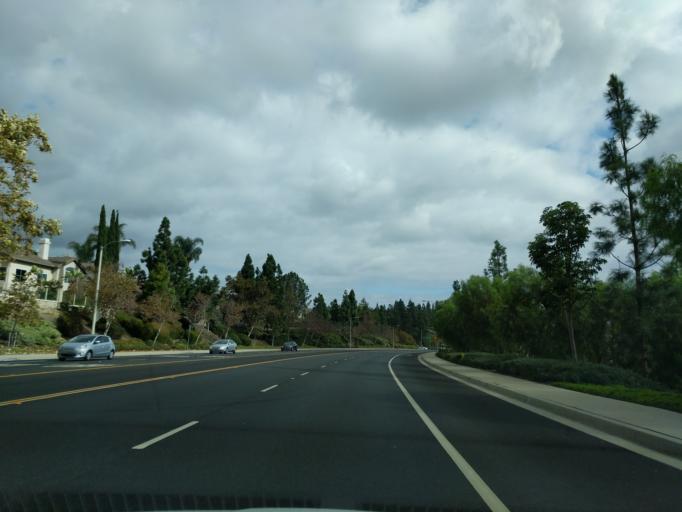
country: US
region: California
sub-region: Orange County
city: Aliso Viejo
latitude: 33.5793
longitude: -117.7399
